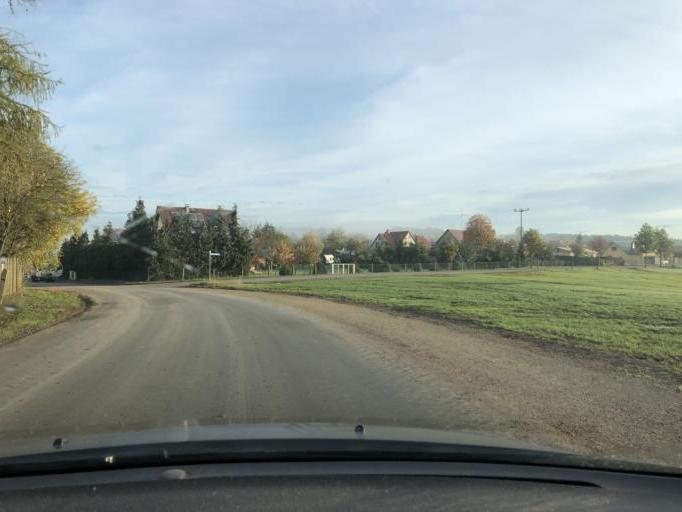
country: DE
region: Thuringia
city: Reurieth
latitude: 50.4161
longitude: 10.6670
